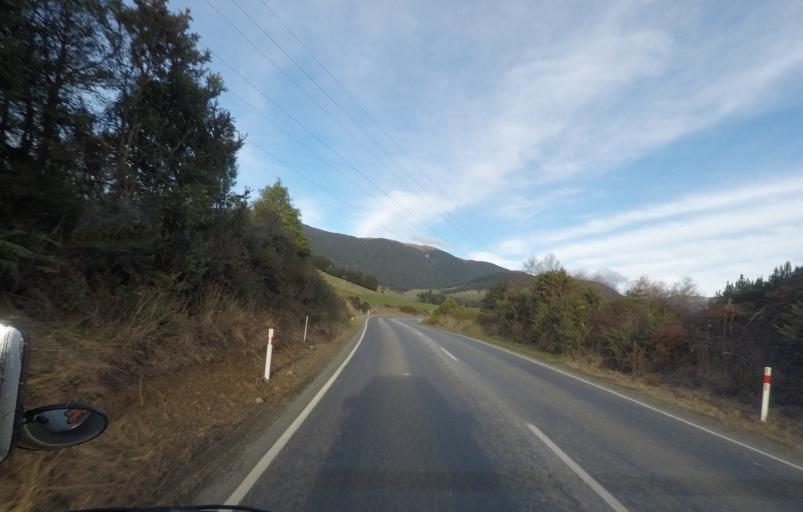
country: NZ
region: Tasman
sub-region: Tasman District
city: Wakefield
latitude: -41.6941
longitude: 172.8847
